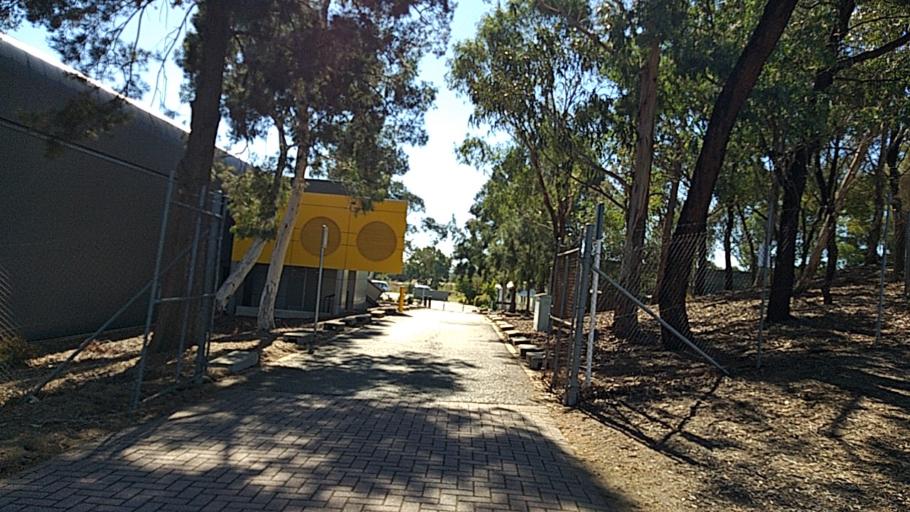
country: AU
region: Australian Capital Territory
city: Kaleen
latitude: -35.2456
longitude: 149.1045
